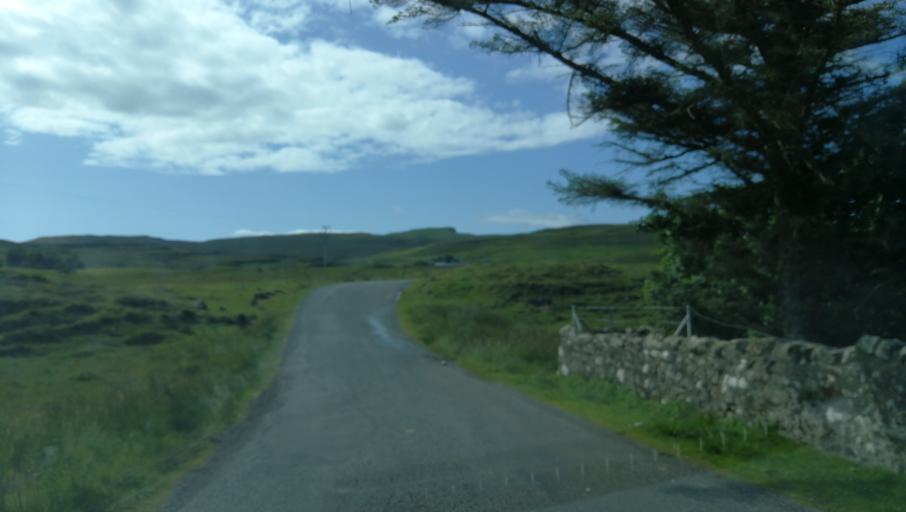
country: GB
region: Scotland
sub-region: Eilean Siar
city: Harris
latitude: 57.4453
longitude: -6.7243
